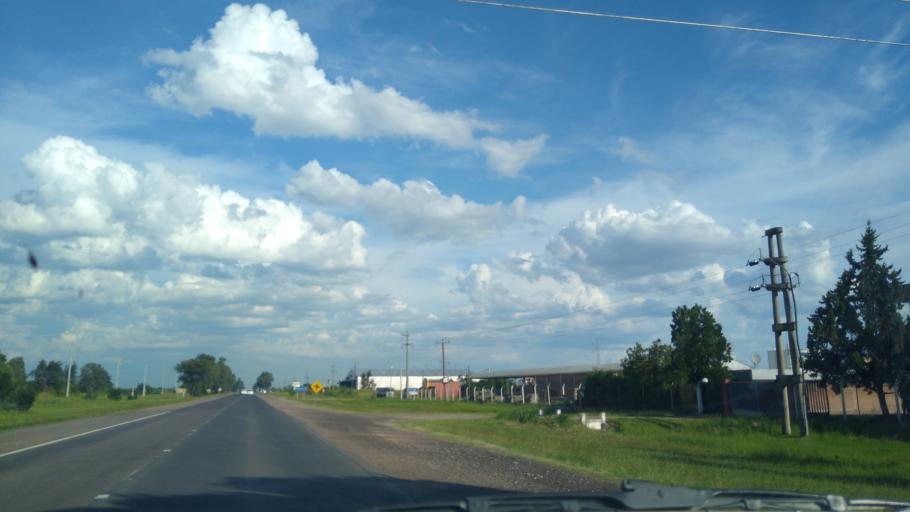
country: AR
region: Chaco
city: Presidencia Roque Saenz Pena
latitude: -26.8152
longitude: -60.4108
